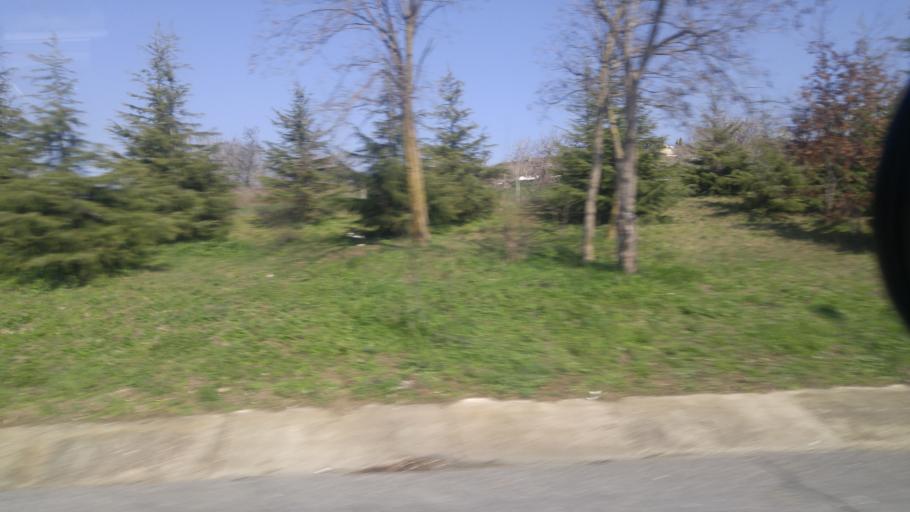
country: TR
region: Istanbul
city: Celaliye
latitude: 41.0602
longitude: 28.4109
